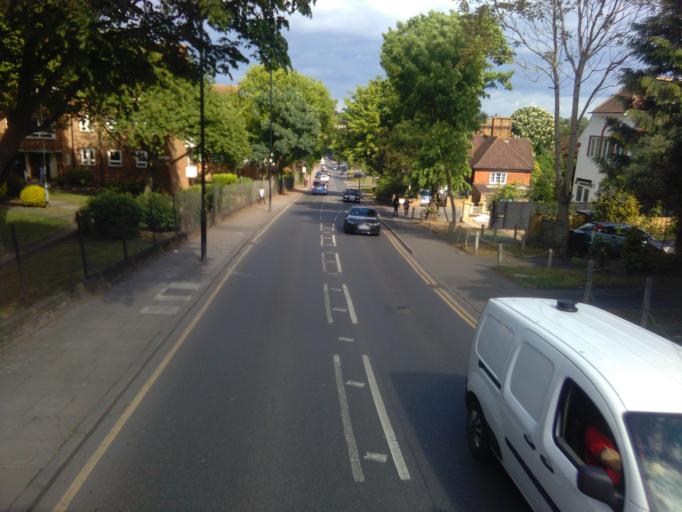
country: GB
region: England
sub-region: Greater London
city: Thornton Heath
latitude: 51.4228
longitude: -0.1047
